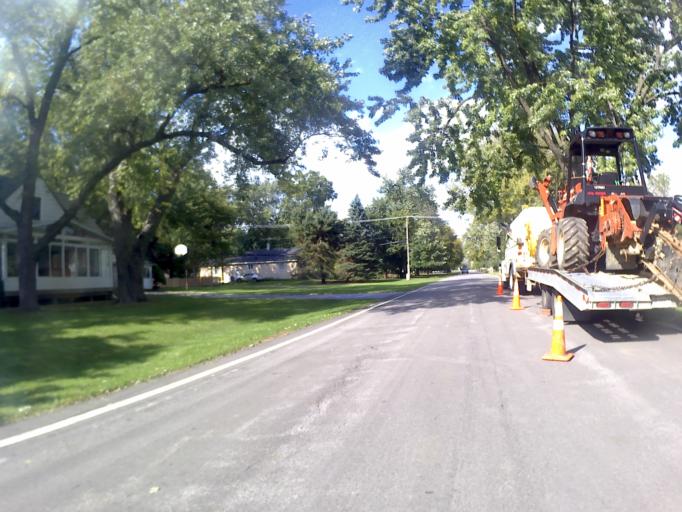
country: US
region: Illinois
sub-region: DuPage County
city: Lisle
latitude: 41.7975
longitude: -88.0822
